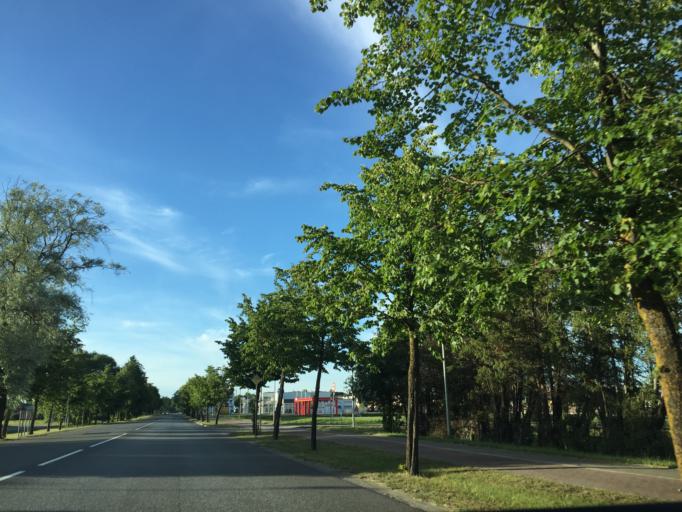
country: LV
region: Ventspils
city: Ventspils
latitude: 57.3757
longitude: 21.5658
